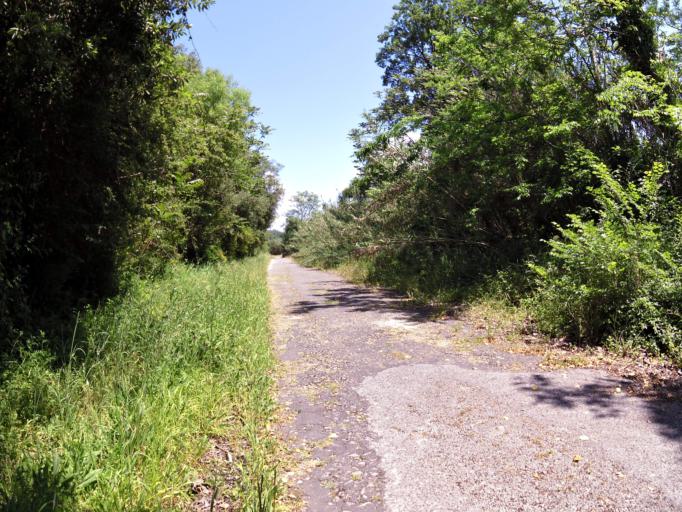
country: PT
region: Coimbra
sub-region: Montemor-O-Velho
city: Montemor-o-Velho
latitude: 40.1736
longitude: -8.6999
